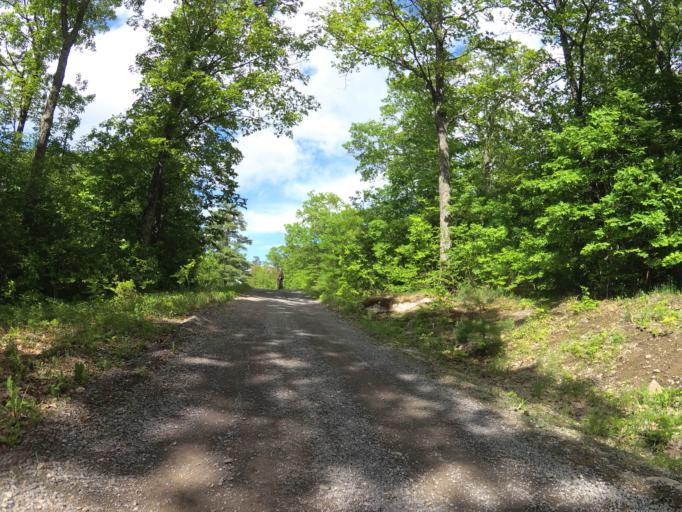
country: CA
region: Ontario
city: Renfrew
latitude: 45.1215
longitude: -76.8838
